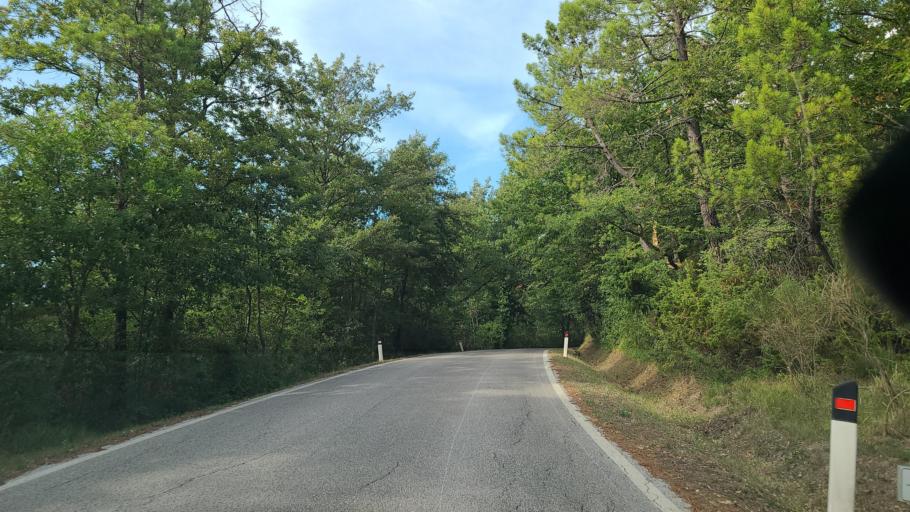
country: IT
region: Tuscany
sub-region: Provincia di Siena
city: San Gimignano
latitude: 43.4306
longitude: 10.9681
